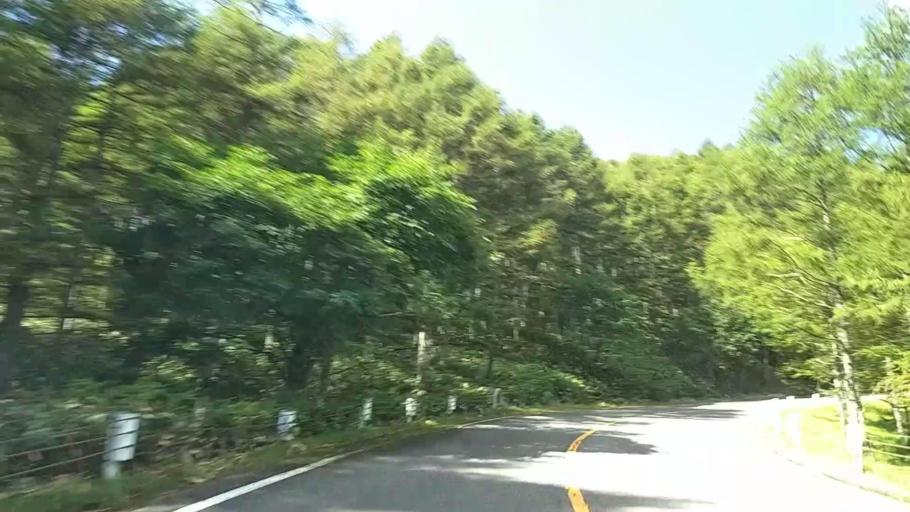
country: JP
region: Nagano
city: Suwa
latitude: 36.1533
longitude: 138.1379
